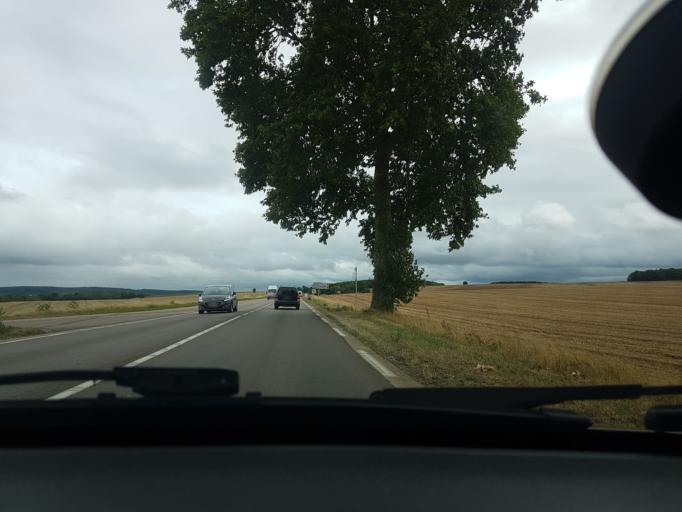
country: FR
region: Bourgogne
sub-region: Departement de l'Yonne
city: Saint-Bris-le-Vineux
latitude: 47.6927
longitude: 3.6460
